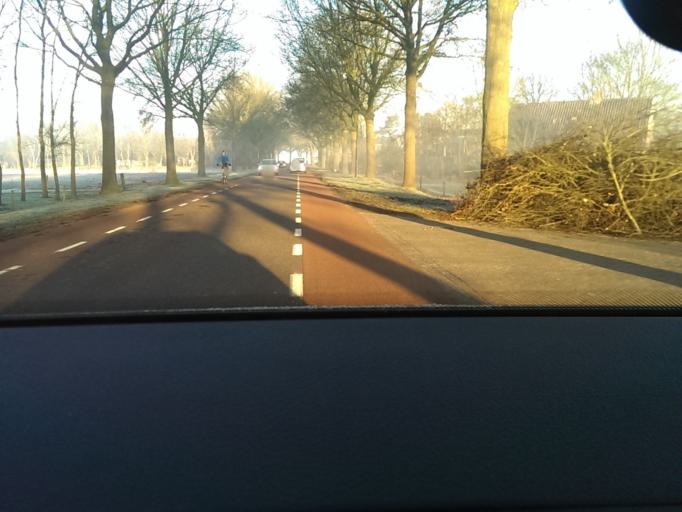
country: NL
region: Overijssel
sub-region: Gemeente Twenterand
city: Vroomshoop
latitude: 52.4073
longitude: 6.5665
